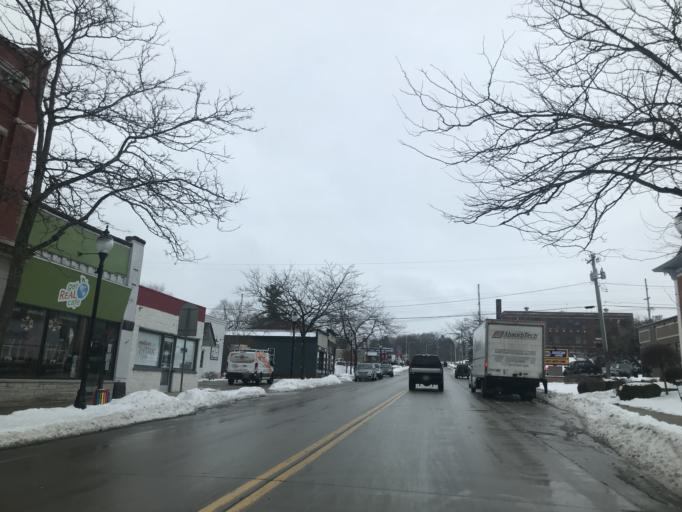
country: US
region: Wisconsin
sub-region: Door County
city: Sturgeon Bay
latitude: 44.8279
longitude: -87.3845
